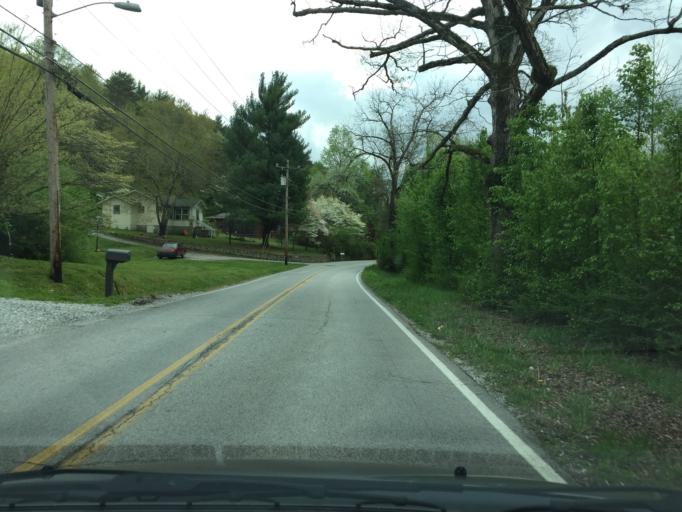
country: US
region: Tennessee
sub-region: Hamilton County
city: Falling Water
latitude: 35.1561
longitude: -85.2455
